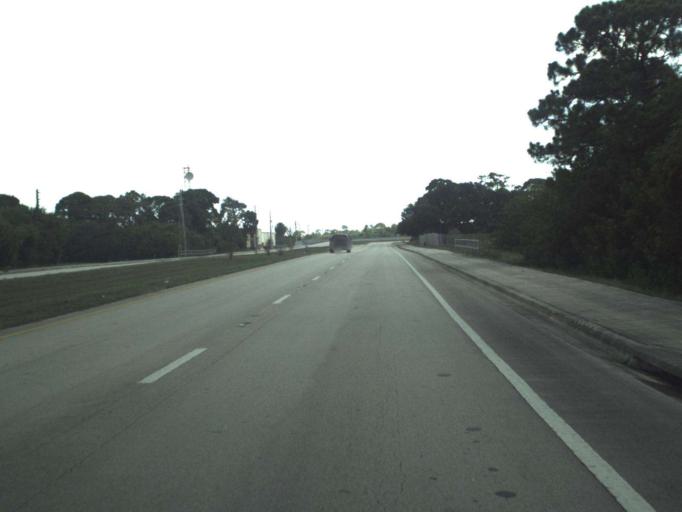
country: US
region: Florida
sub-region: Saint Lucie County
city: Fort Pierce North
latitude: 27.4914
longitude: -80.3496
